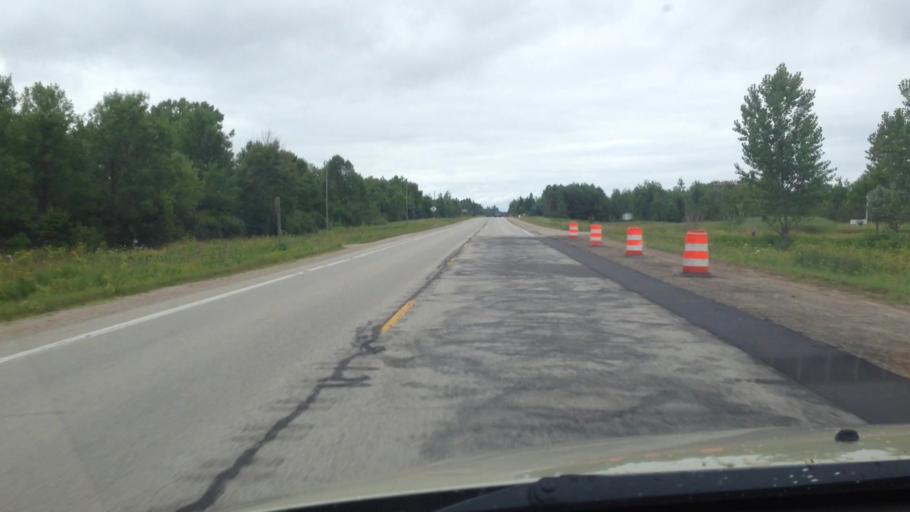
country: US
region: Michigan
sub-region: Delta County
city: Escanaba
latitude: 45.5602
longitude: -87.2622
